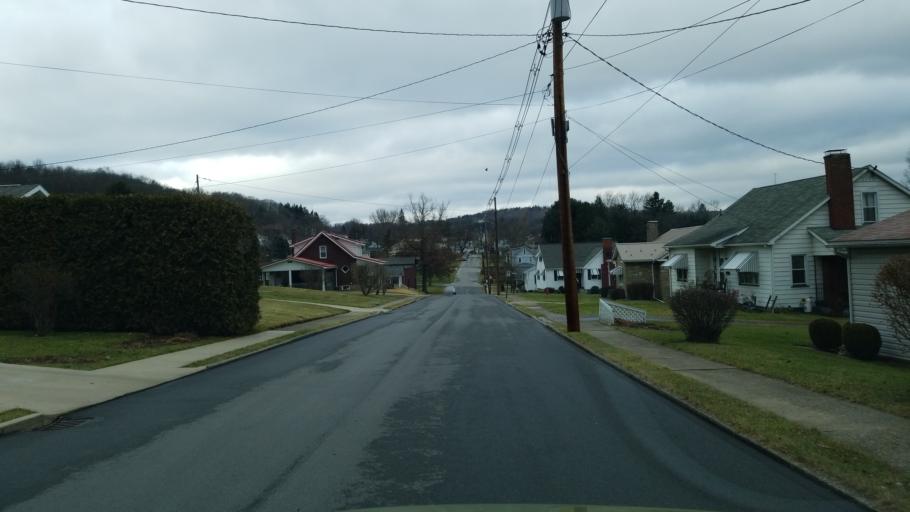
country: US
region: Pennsylvania
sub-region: Clearfield County
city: Clearfield
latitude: 41.0275
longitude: -78.4514
